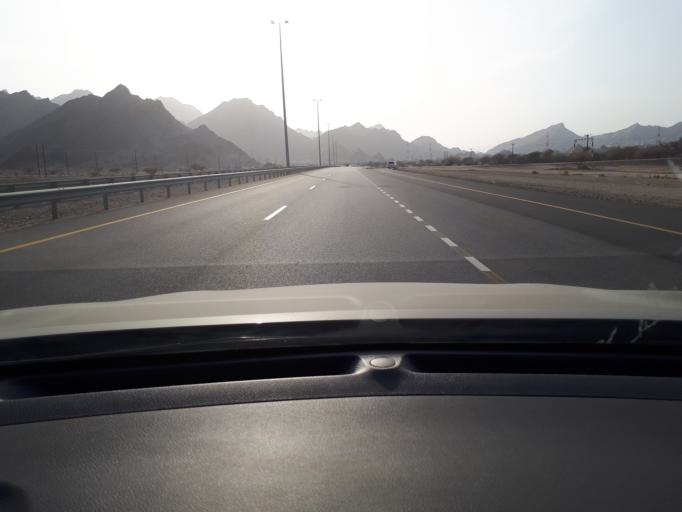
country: OM
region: Muhafazat Masqat
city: Muscat
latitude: 23.3664
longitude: 58.6519
